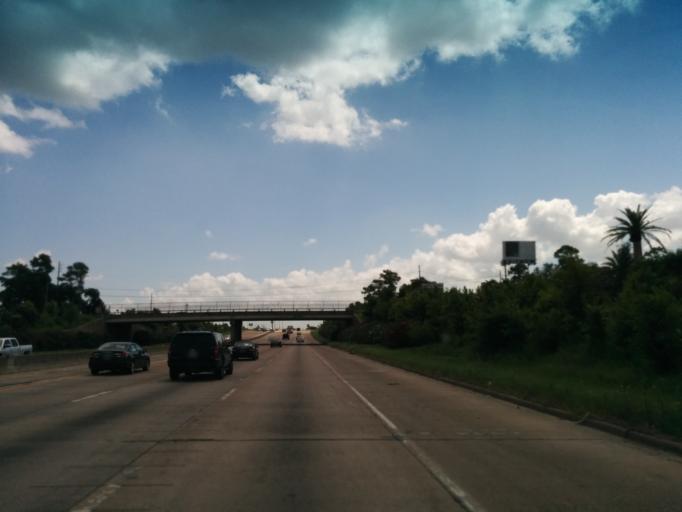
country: US
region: Texas
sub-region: Harris County
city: Channelview
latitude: 29.7856
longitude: -95.1048
